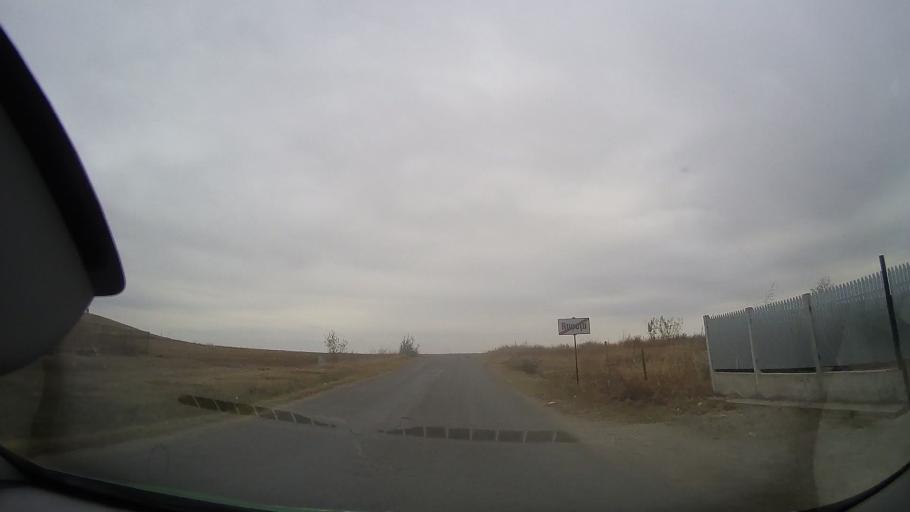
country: RO
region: Buzau
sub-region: Comuna Rusetu
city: Rusetu
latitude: 44.9649
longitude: 27.2053
